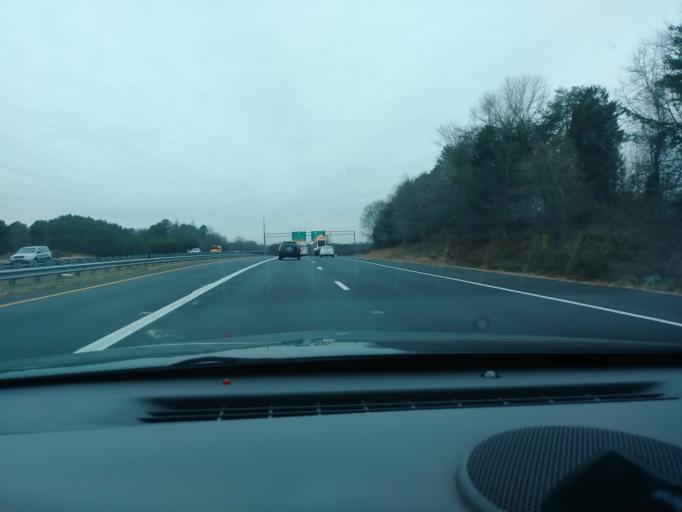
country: US
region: North Carolina
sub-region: Forsyth County
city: Winston-Salem
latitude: 36.0755
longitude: -80.3202
